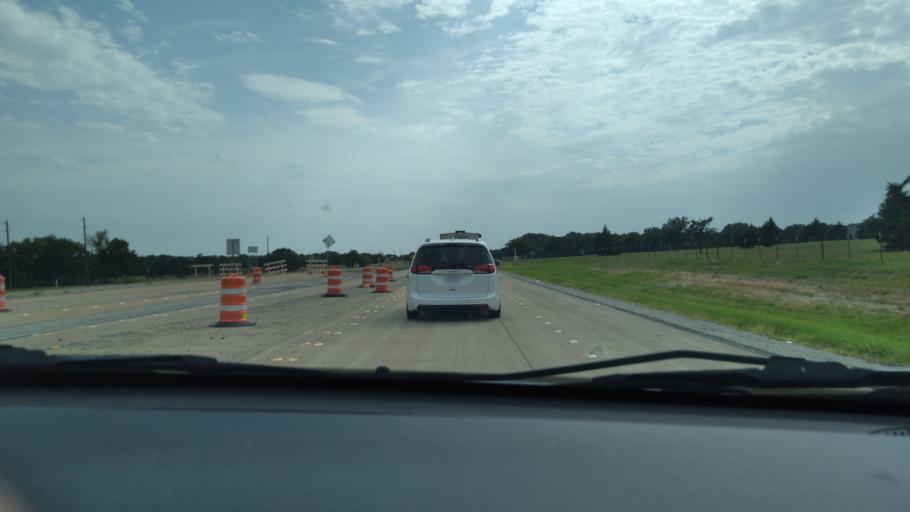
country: US
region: Texas
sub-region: Hill County
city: Hubbard
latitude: 31.8772
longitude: -96.7575
